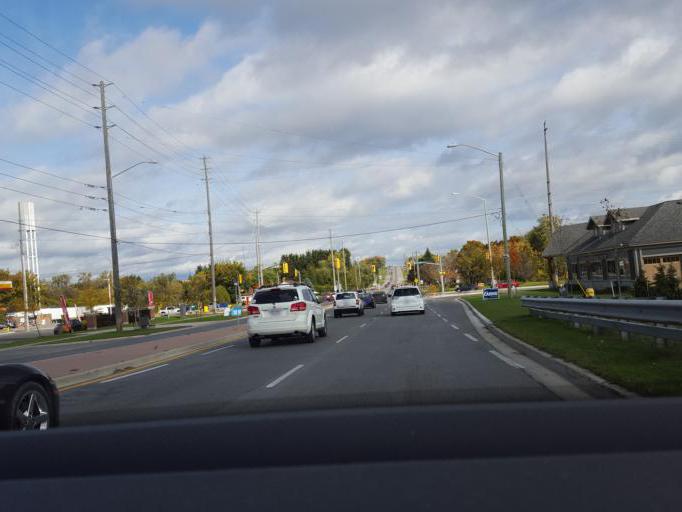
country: CA
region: Ontario
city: Oshawa
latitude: 43.9436
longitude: -78.8311
